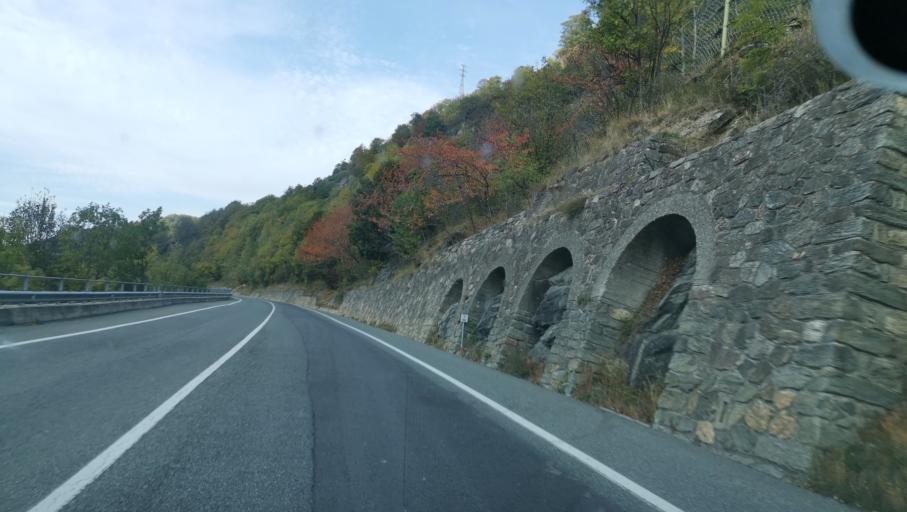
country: IT
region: Piedmont
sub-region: Provincia di Torino
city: Exilles
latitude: 45.0937
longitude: 6.9215
